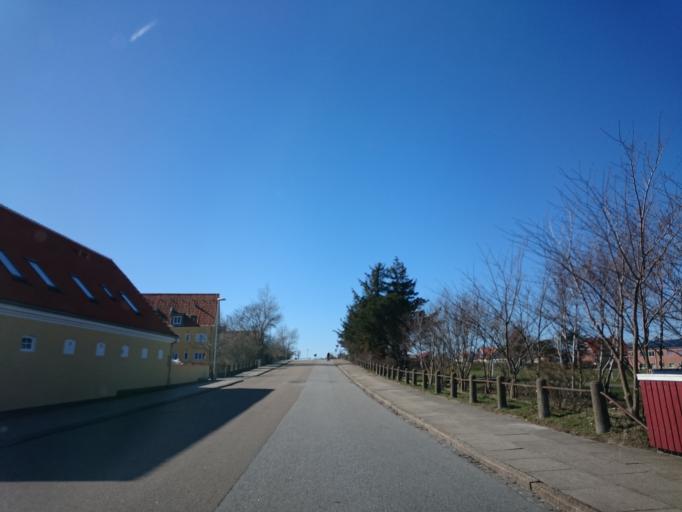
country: DK
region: North Denmark
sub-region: Frederikshavn Kommune
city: Skagen
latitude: 57.7256
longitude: 10.5852
